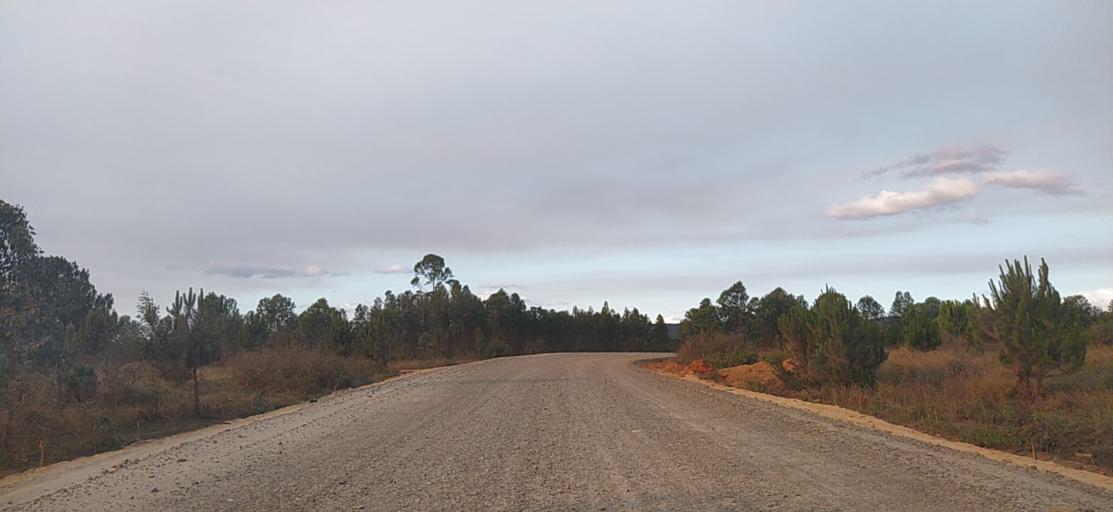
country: MG
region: Analamanga
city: Anjozorobe
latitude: -18.5062
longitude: 48.2638
